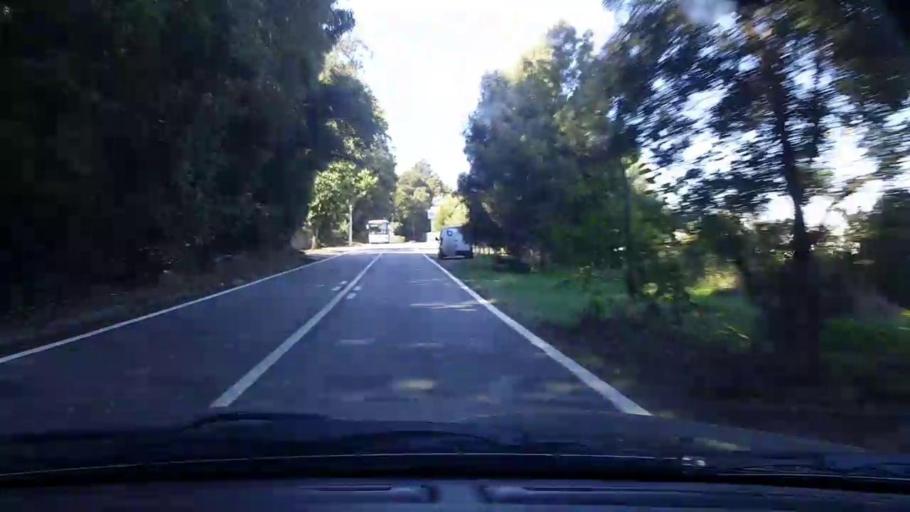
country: PT
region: Porto
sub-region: Vila do Conde
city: Arvore
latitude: 41.3409
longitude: -8.6503
